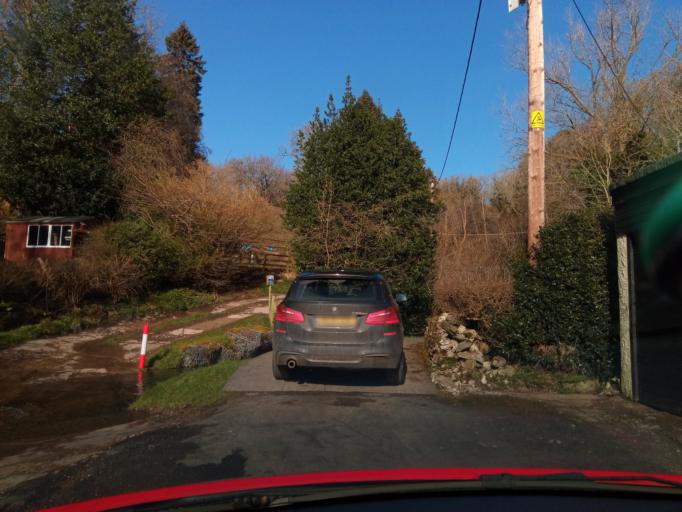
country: GB
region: Scotland
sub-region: The Scottish Borders
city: Hawick
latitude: 55.4245
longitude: -2.8080
